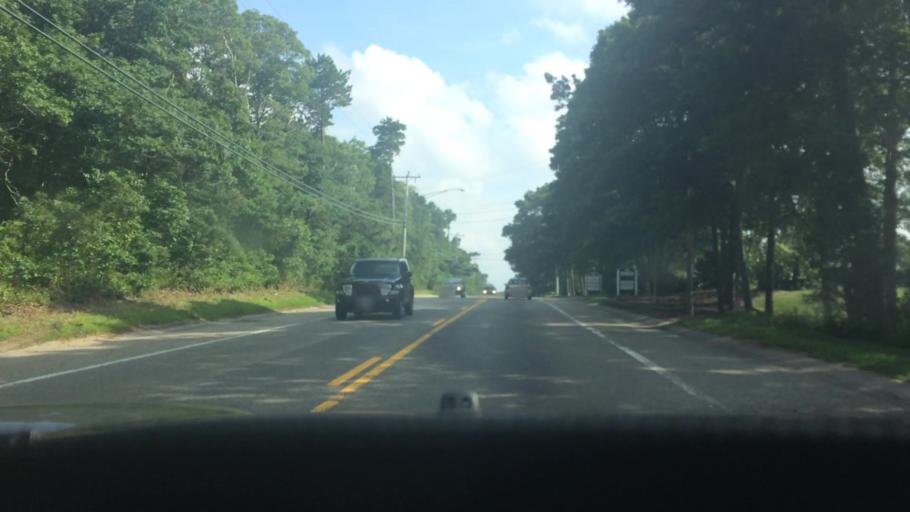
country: US
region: Massachusetts
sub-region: Barnstable County
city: Sandwich
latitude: 41.7347
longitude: -70.4916
